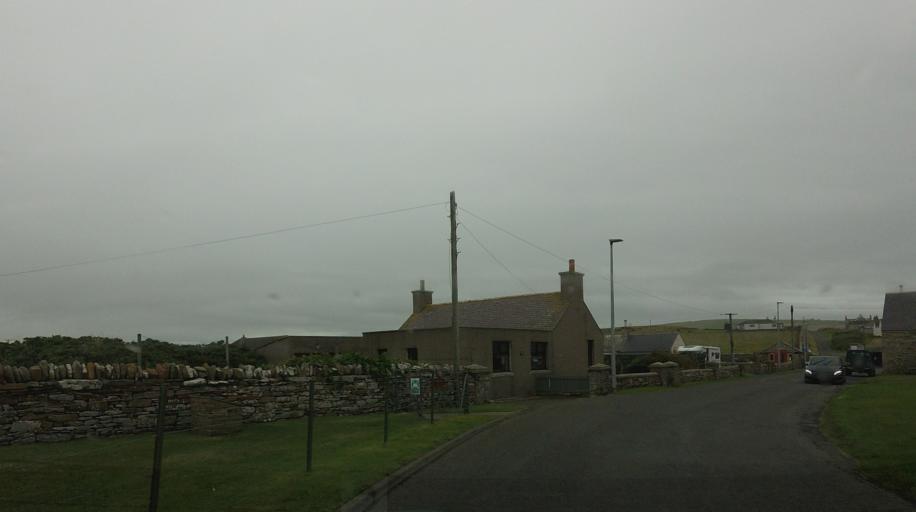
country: GB
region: Scotland
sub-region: Orkney Islands
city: Stromness
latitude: 59.1296
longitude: -3.3156
